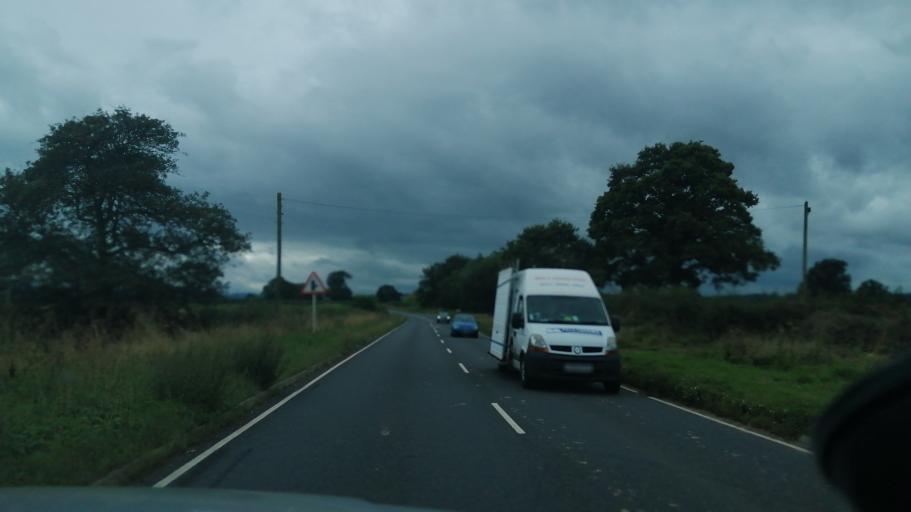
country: GB
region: England
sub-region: Herefordshire
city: Thruxton
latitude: 52.0099
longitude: -2.7897
